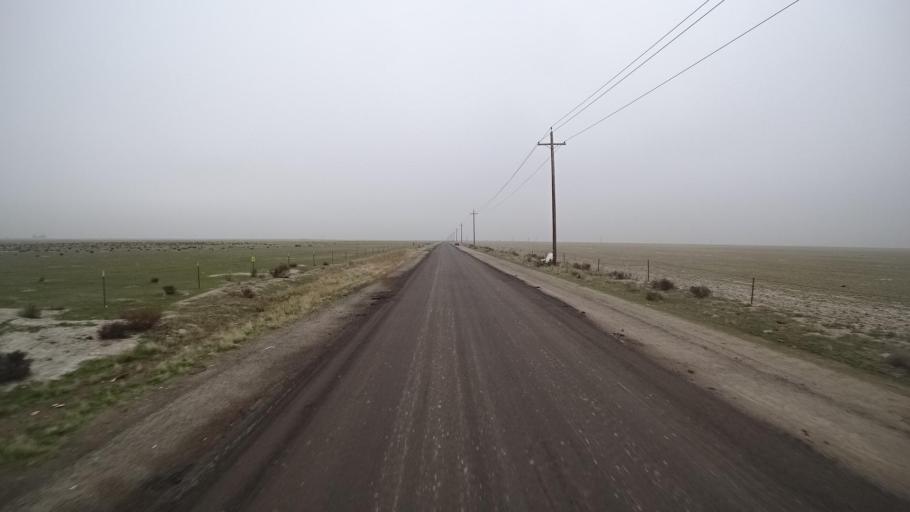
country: US
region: California
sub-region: Tulare County
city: Alpaugh
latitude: 35.7804
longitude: -119.4723
